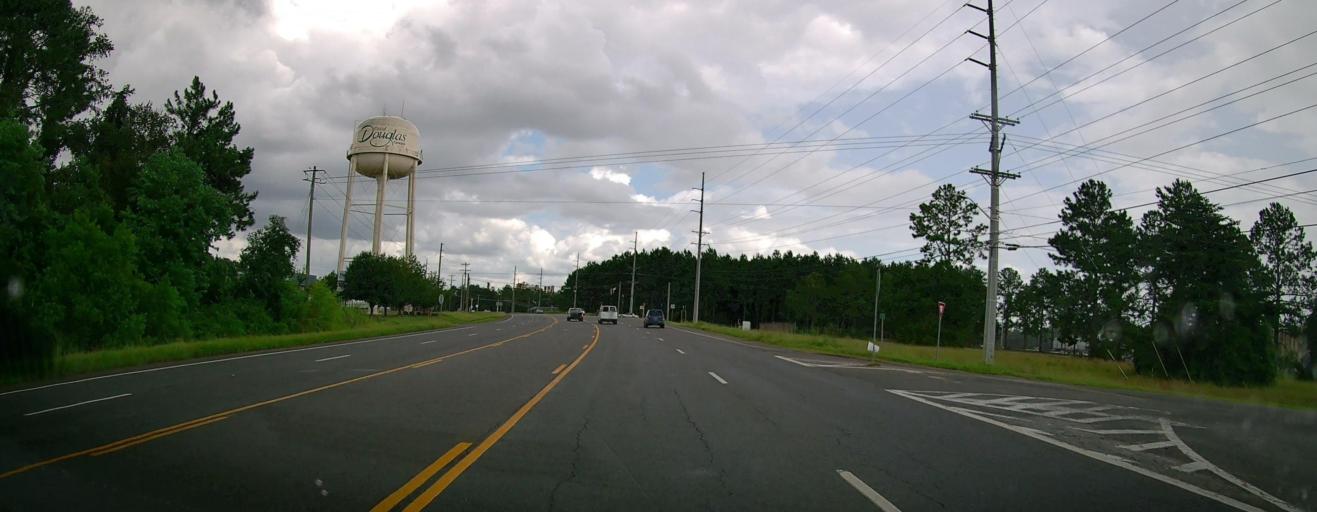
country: US
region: Georgia
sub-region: Coffee County
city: Douglas
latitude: 31.4902
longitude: -82.8684
